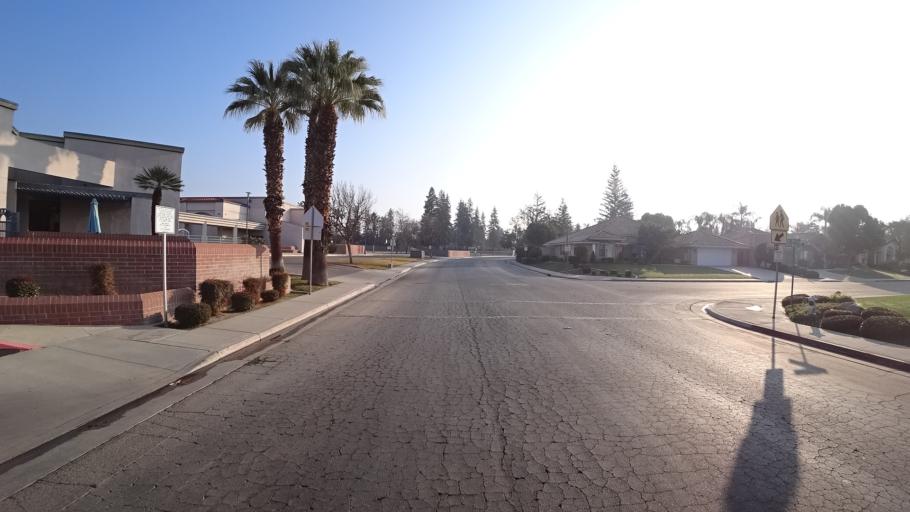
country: US
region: California
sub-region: Kern County
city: Greenacres
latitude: 35.3304
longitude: -119.1012
